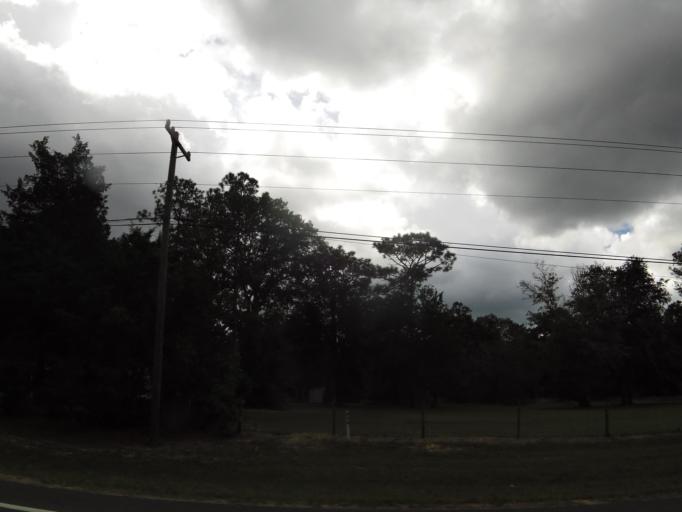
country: US
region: Florida
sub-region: Clay County
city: Middleburg
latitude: 30.0458
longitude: -81.8478
